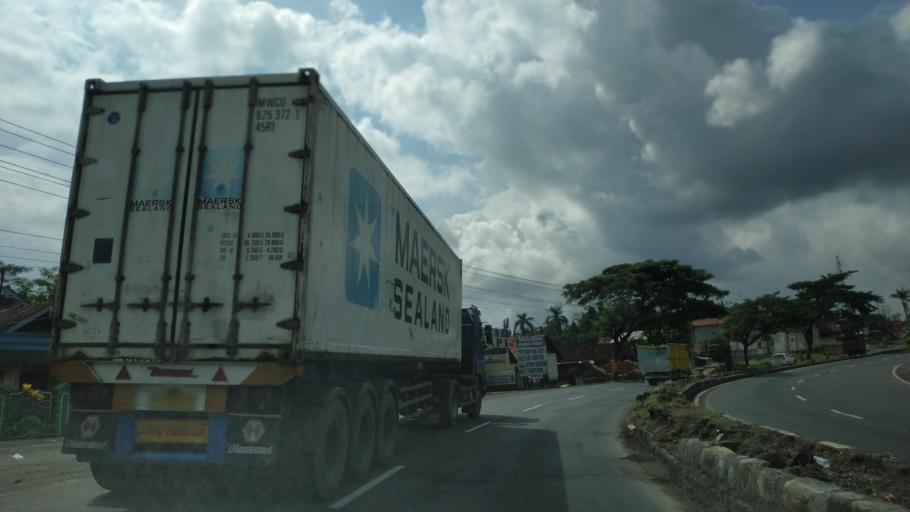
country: ID
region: Central Java
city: Pekalongan
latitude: -6.9447
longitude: 109.8193
